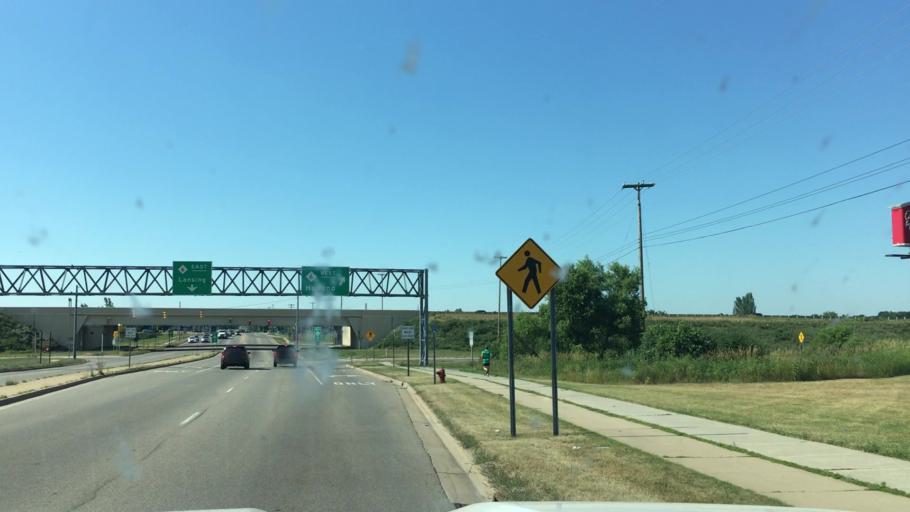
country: US
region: Michigan
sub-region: Kent County
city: Kentwood
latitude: 42.8489
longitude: -85.6250
